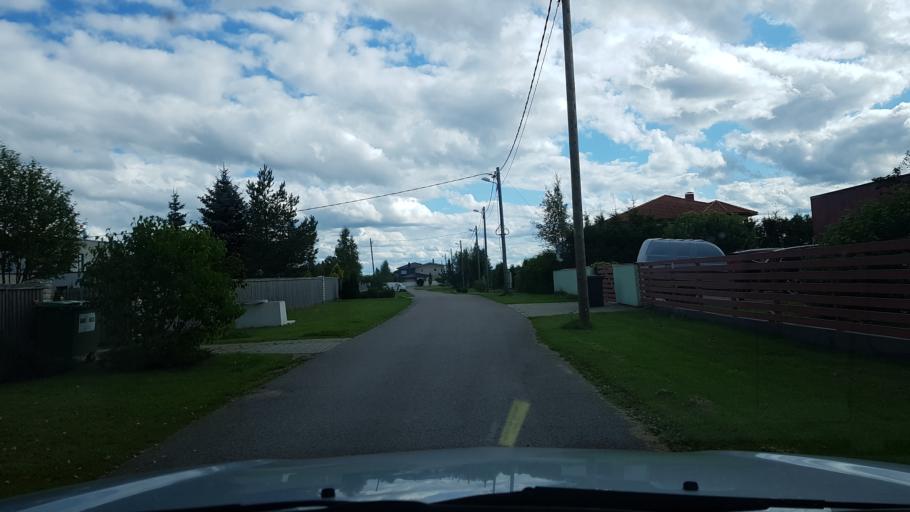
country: EE
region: Harju
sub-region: Tallinna linn
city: Tallinn
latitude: 59.3825
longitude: 24.8109
